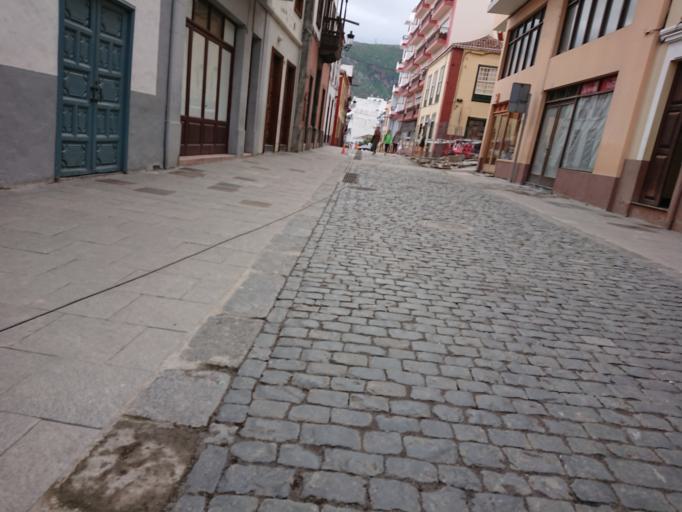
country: ES
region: Canary Islands
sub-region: Provincia de Santa Cruz de Tenerife
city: Santa Cruz de la Palma
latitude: 28.6865
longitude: -17.7617
